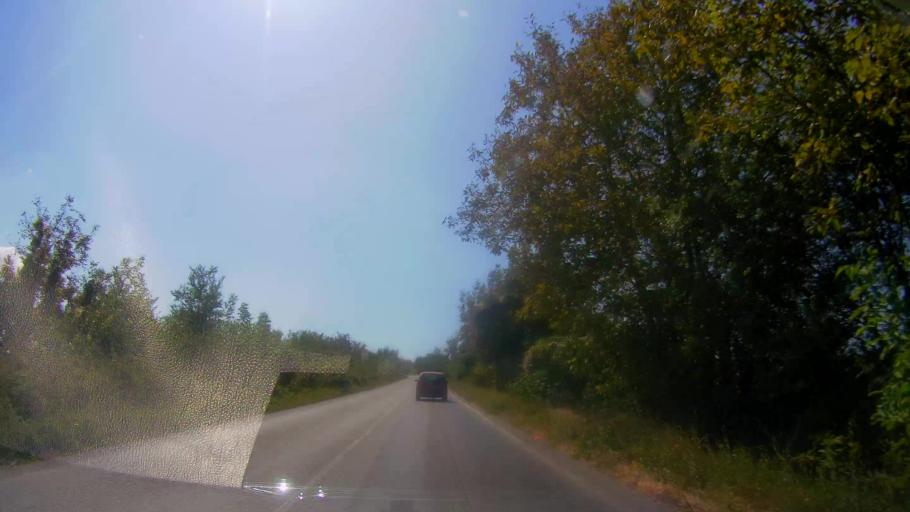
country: BG
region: Veliko Turnovo
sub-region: Obshtina Gorna Oryakhovitsa
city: Purvomaytsi
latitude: 43.2593
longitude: 25.6425
